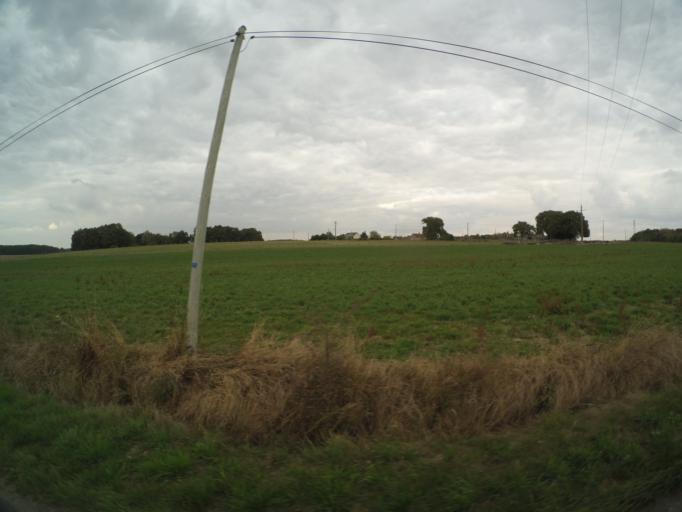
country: FR
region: Centre
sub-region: Departement d'Indre-et-Loire
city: Reugny
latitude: 47.4953
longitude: 0.9304
